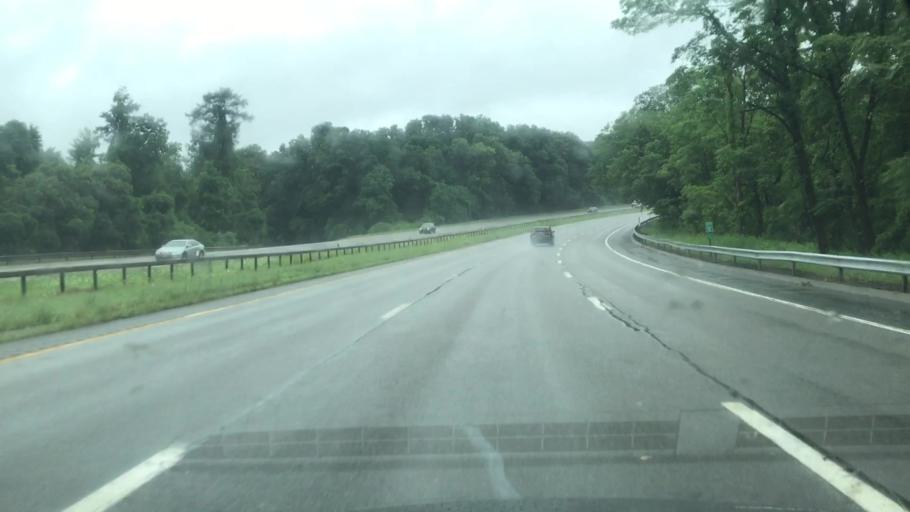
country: US
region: New York
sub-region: Westchester County
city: Yorktown Heights
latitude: 41.2776
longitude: -73.8184
